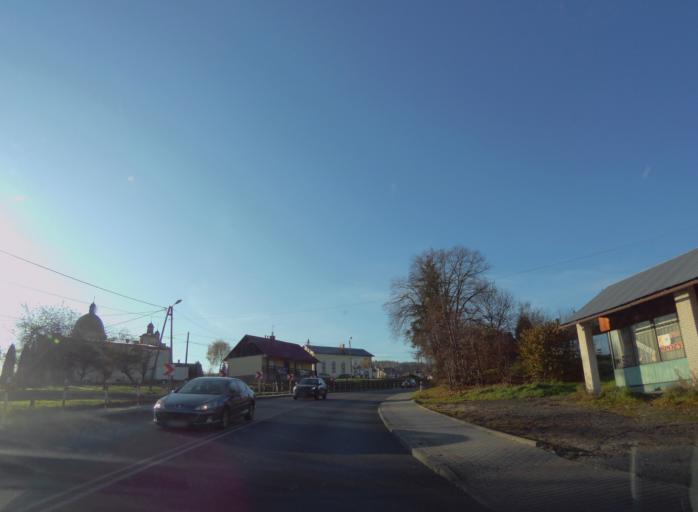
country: PL
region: Subcarpathian Voivodeship
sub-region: Powiat strzyzowski
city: Niebylec
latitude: 49.8574
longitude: 21.9038
